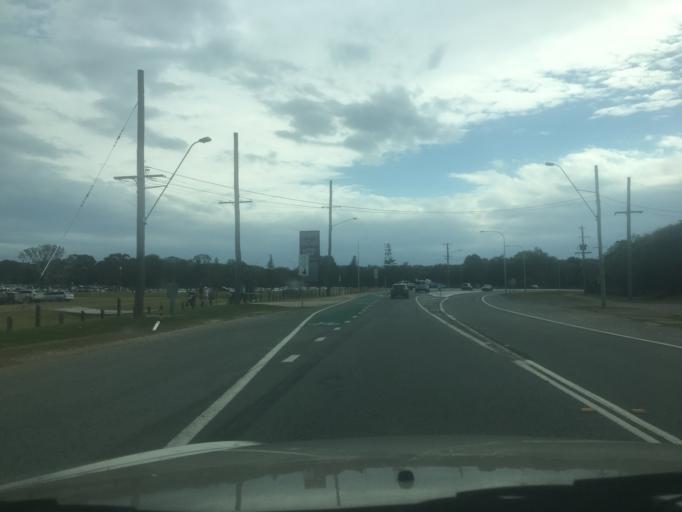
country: AU
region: Queensland
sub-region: Moreton Bay
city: Bongaree
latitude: -27.0736
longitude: 153.1418
